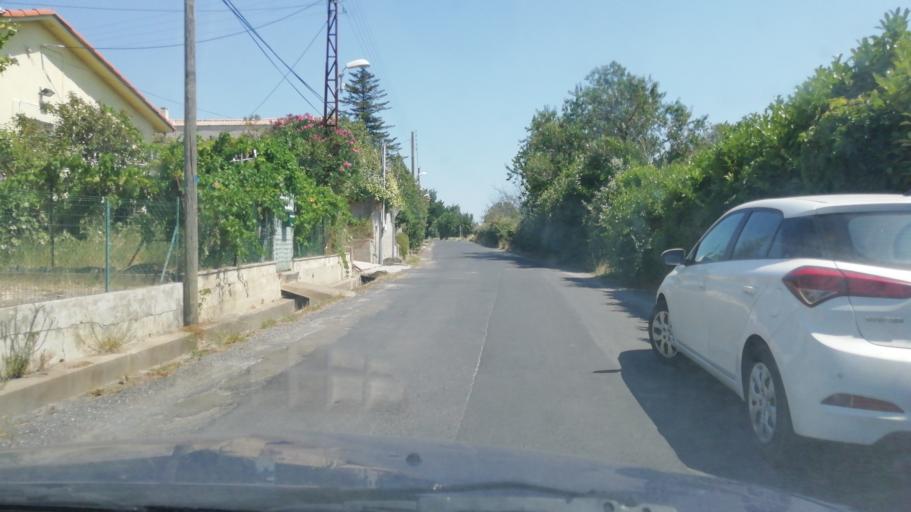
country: FR
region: Languedoc-Roussillon
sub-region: Departement de l'Herault
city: Capestang
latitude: 43.3311
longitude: 3.0470
